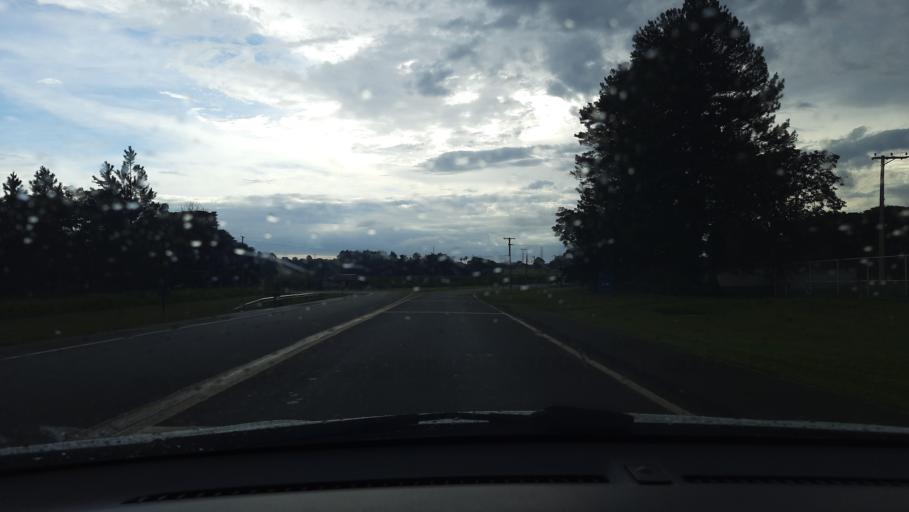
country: BR
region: Sao Paulo
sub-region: Casa Branca
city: Casa Branca
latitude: -21.7730
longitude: -47.0580
